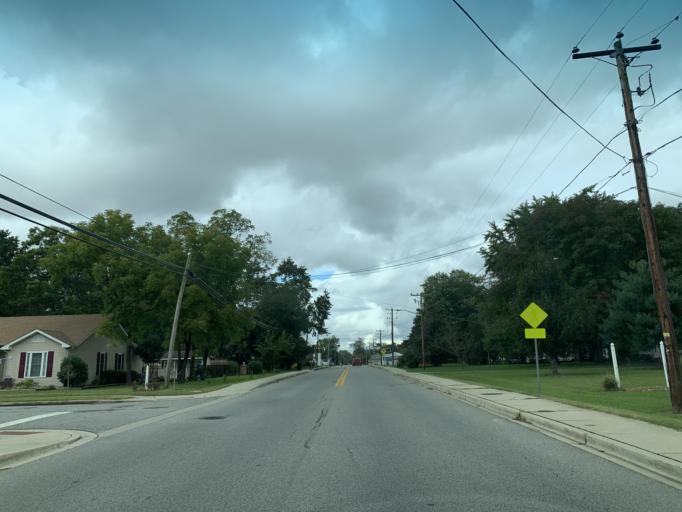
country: US
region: Maryland
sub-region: Caroline County
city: Denton
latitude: 38.8766
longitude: -75.8272
